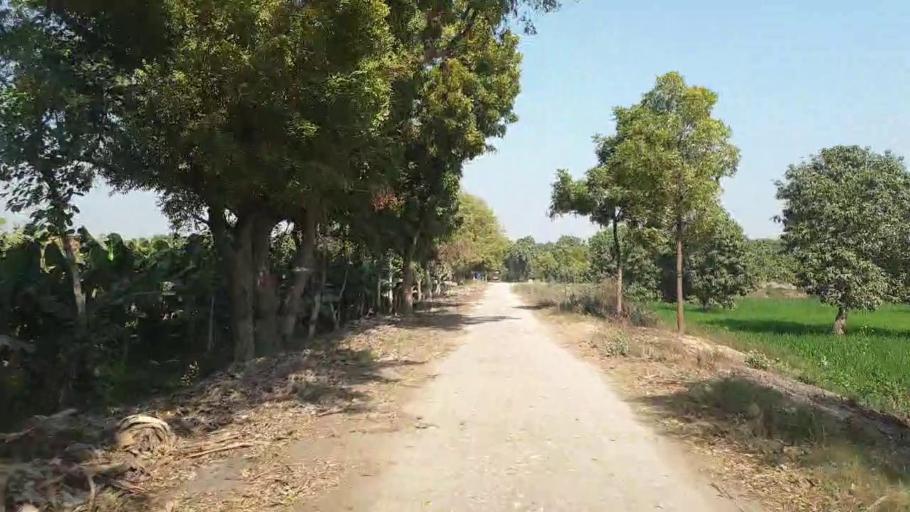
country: PK
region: Sindh
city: Tando Jam
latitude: 25.3429
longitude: 68.6139
